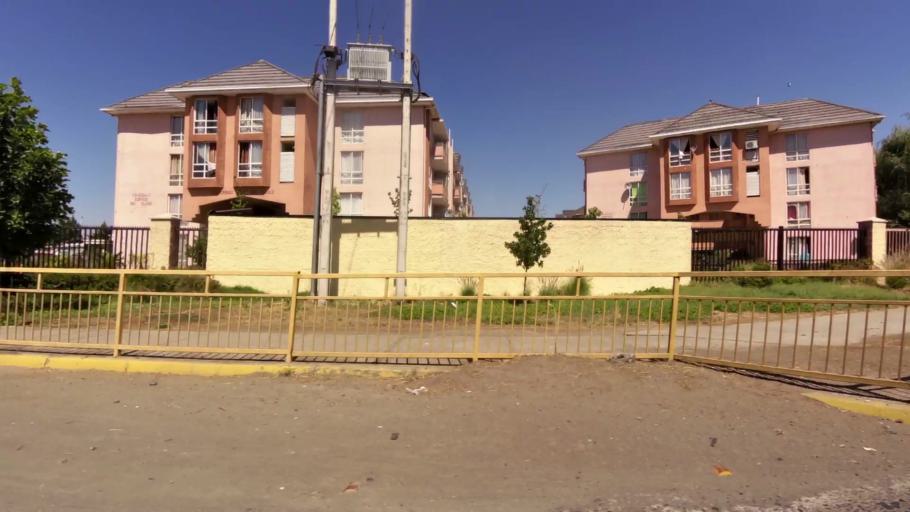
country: CL
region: Maule
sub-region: Provincia de Talca
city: Talca
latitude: -35.4095
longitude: -71.6484
